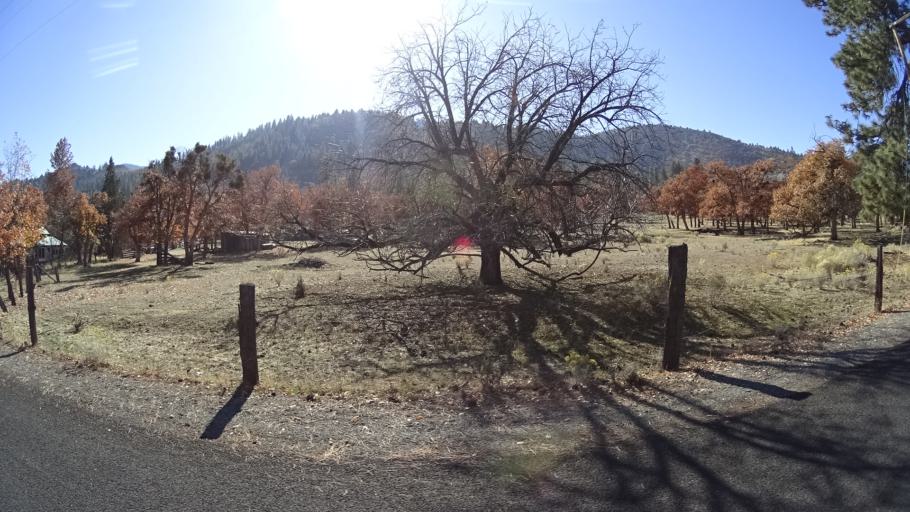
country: US
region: California
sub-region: Siskiyou County
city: Weed
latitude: 41.5035
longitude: -122.5708
